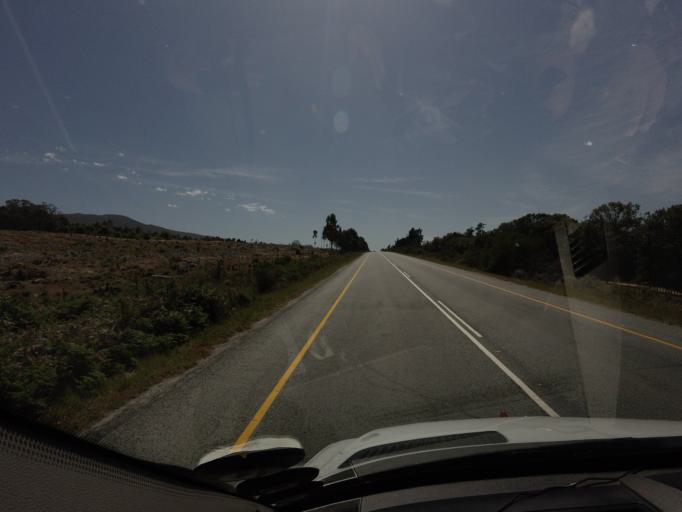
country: ZA
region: Western Cape
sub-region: Overberg District Municipality
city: Hermanus
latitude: -34.3156
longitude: 19.1232
